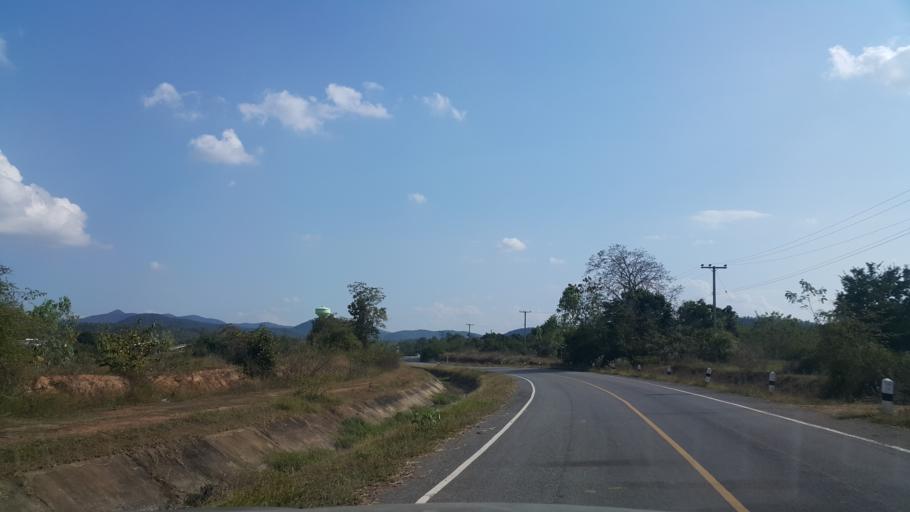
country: TH
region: Lamphun
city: Mae Tha
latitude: 18.5308
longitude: 99.0980
